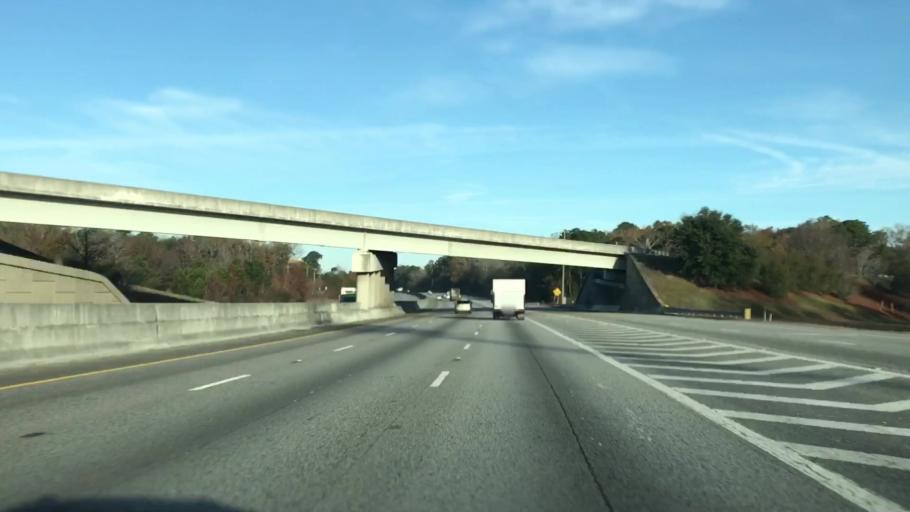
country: US
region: South Carolina
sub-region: Berkeley County
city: Hanahan
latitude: 32.9400
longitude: -80.0502
